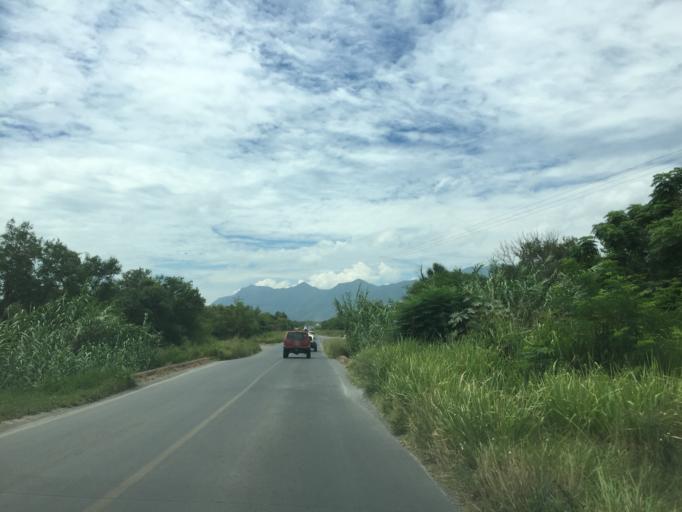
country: MX
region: Nuevo Leon
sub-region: Juarez
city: Bosques de San Pedro
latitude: 25.5335
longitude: -100.1161
